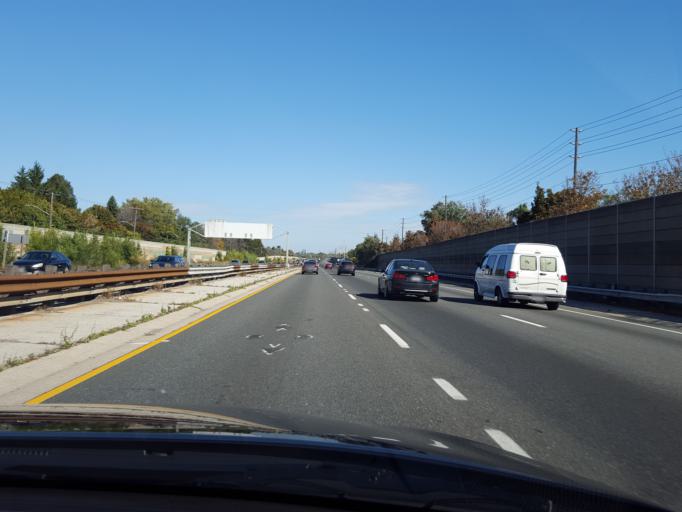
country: CA
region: Ontario
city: Mississauga
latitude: 43.5364
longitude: -79.6344
